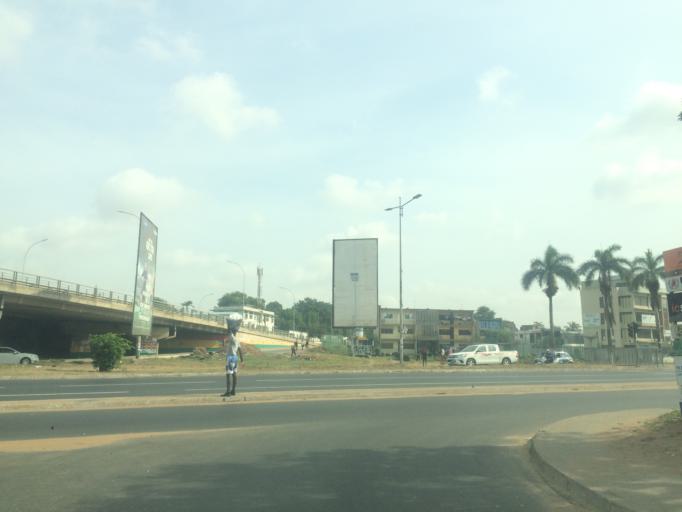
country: GH
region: Greater Accra
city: Accra
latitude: 5.5734
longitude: -0.1984
